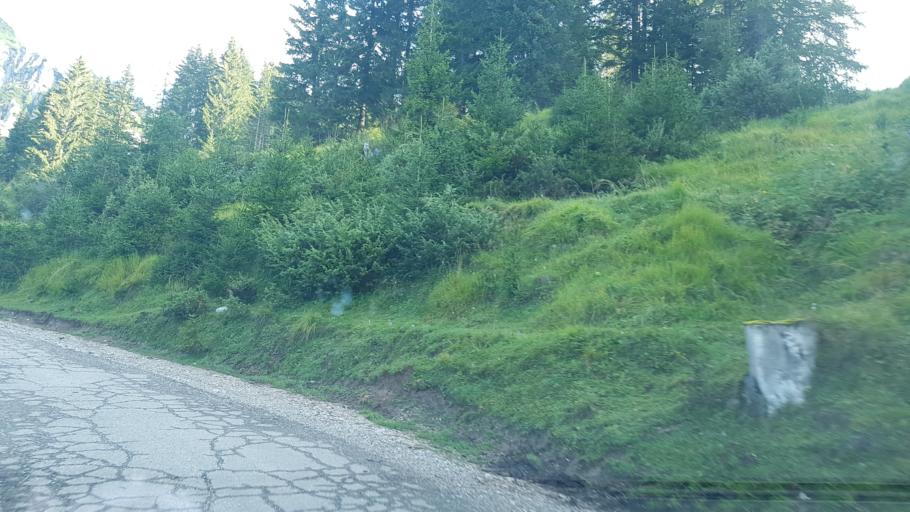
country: IT
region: Veneto
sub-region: Provincia di Belluno
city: San Pietro di Cadore
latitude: 46.6022
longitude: 12.5914
